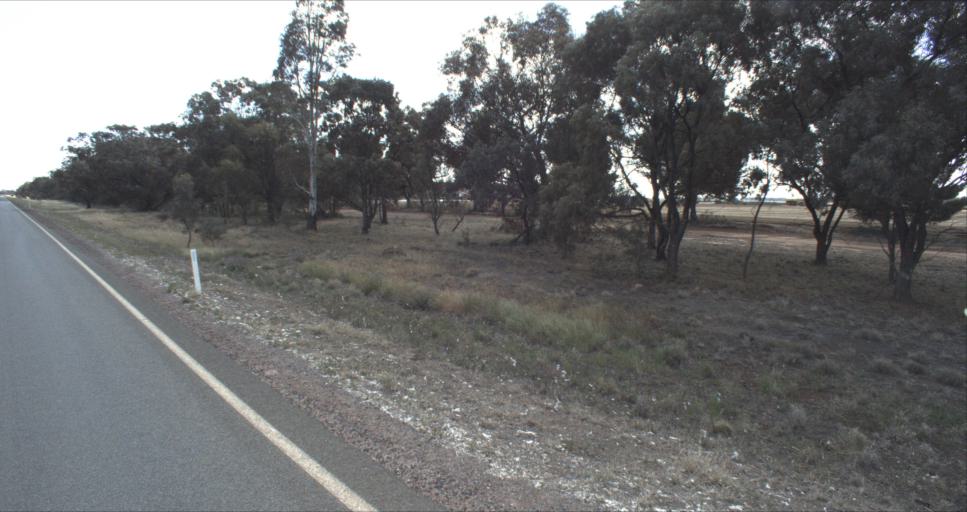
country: AU
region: New South Wales
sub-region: Murrumbidgee Shire
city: Darlington Point
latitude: -34.5920
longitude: 146.1634
